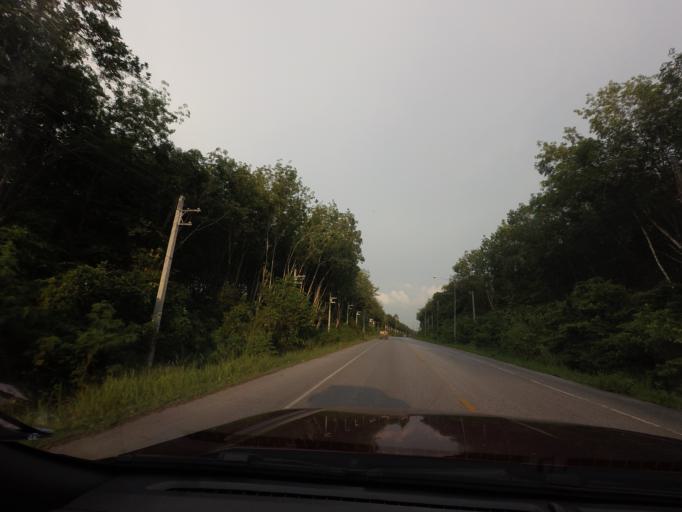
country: TH
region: Pattani
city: Khok Pho
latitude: 6.6732
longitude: 101.1550
